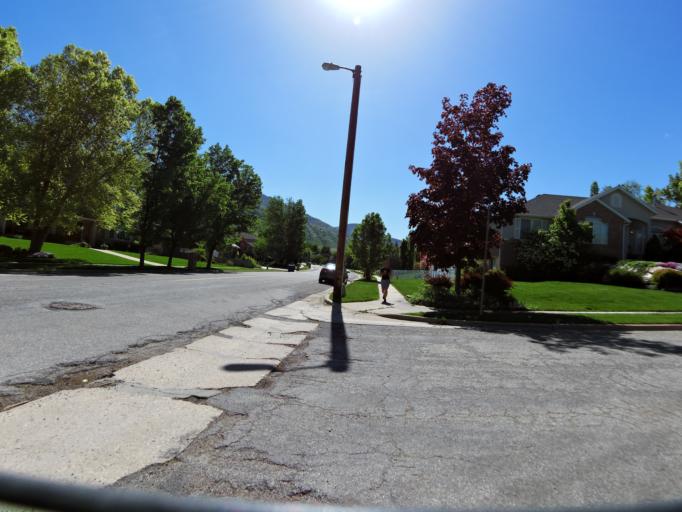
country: US
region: Utah
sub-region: Weber County
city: Uintah
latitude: 41.1673
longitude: -111.9320
